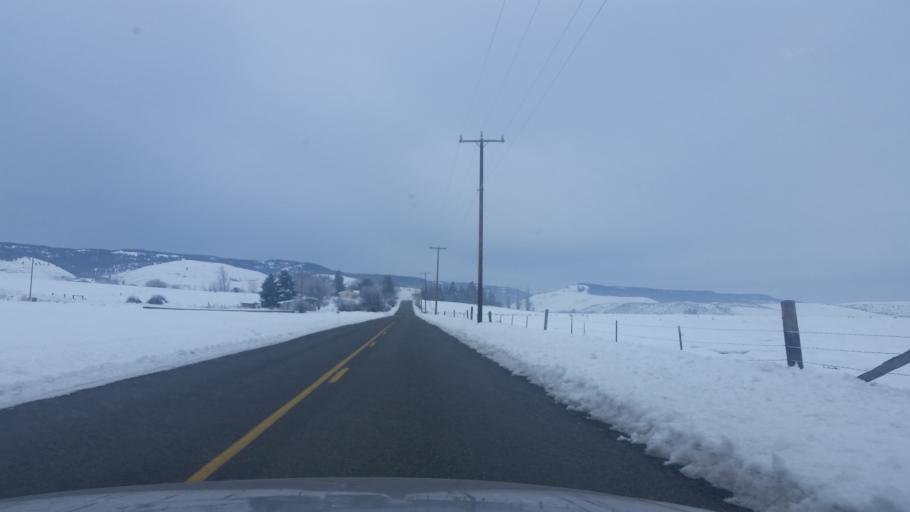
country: US
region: Washington
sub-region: Kittitas County
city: Ellensburg
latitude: 47.0799
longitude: -120.7010
